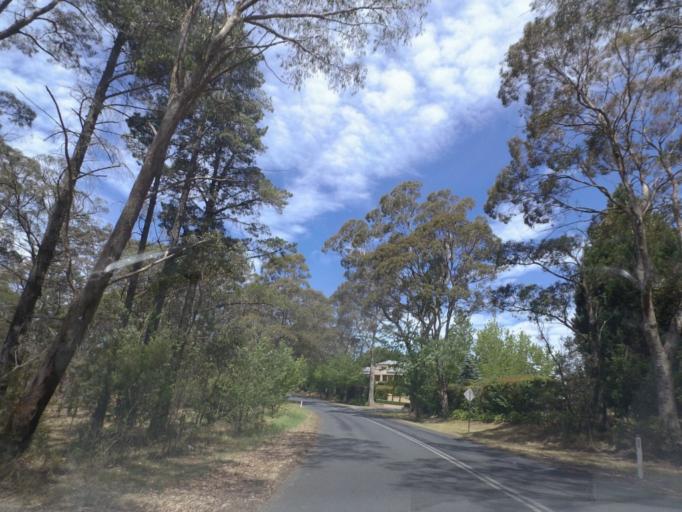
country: AU
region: New South Wales
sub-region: Wingecarribee
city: Colo Vale
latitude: -34.4073
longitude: 150.5140
